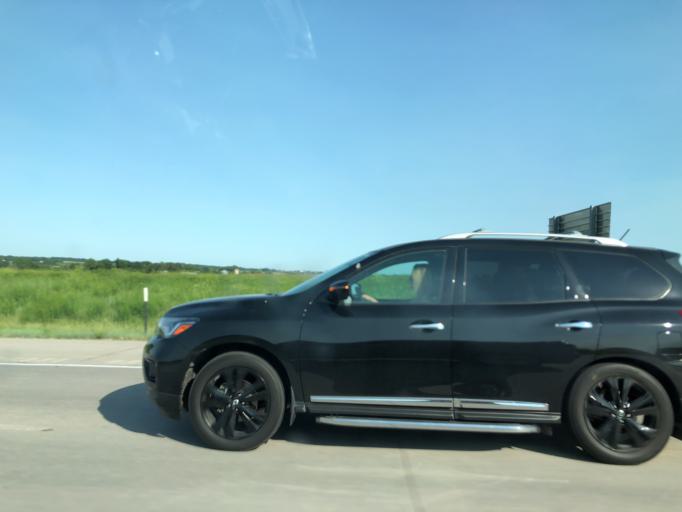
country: US
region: Nebraska
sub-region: Saunders County
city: Ashland
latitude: 40.9792
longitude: -96.3775
